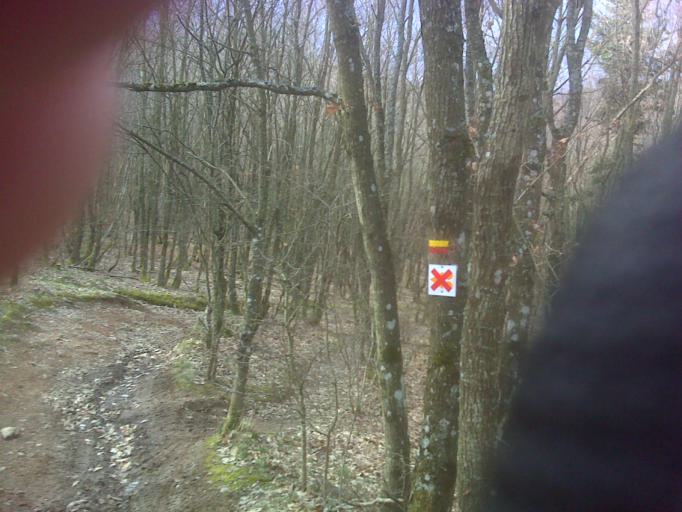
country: FR
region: Rhone-Alpes
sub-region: Departement du Rhone
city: Lentilly
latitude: 45.7950
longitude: 4.6516
